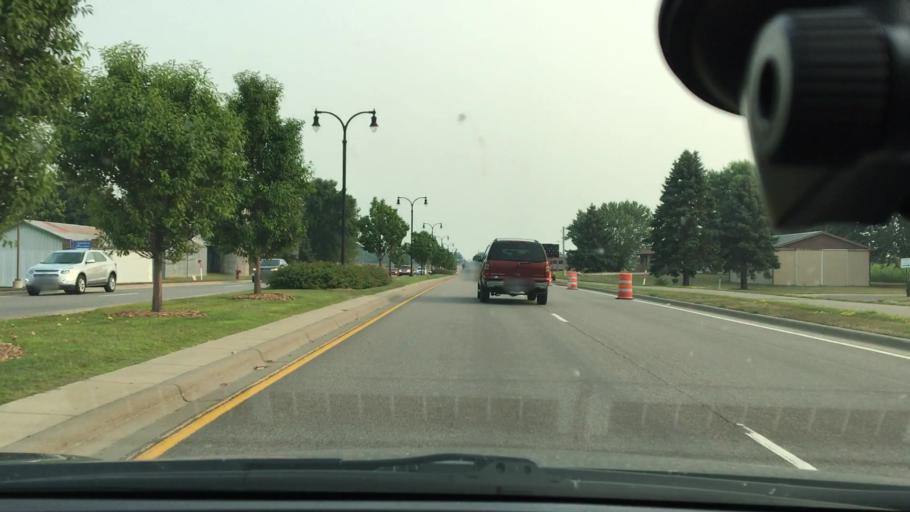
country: US
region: Minnesota
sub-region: Wright County
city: Albertville
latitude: 45.2324
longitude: -93.6644
